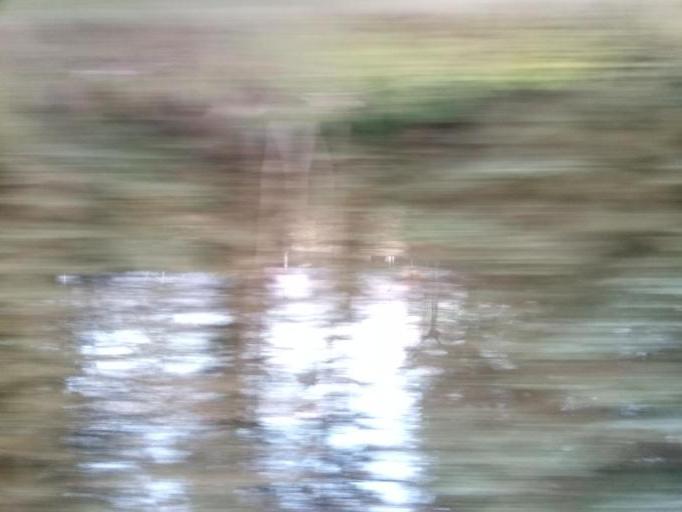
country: GB
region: Scotland
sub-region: East Lothian
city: Pencaitland
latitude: 55.8171
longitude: -2.8465
